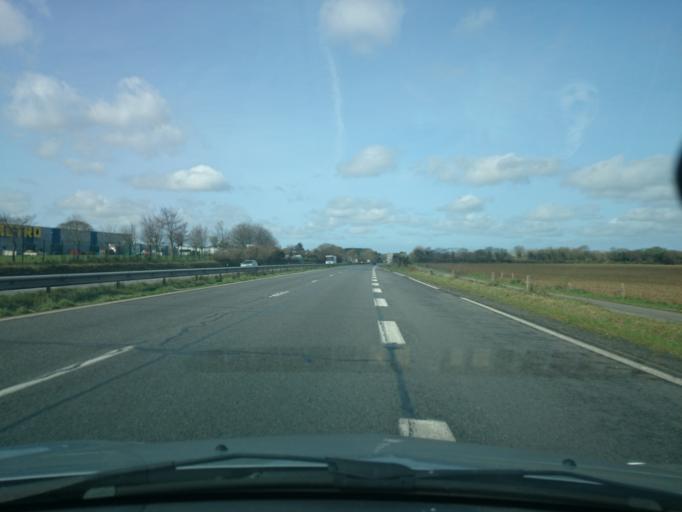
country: FR
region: Brittany
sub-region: Departement du Finistere
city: Gouesnou
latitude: 48.4333
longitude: -4.4502
